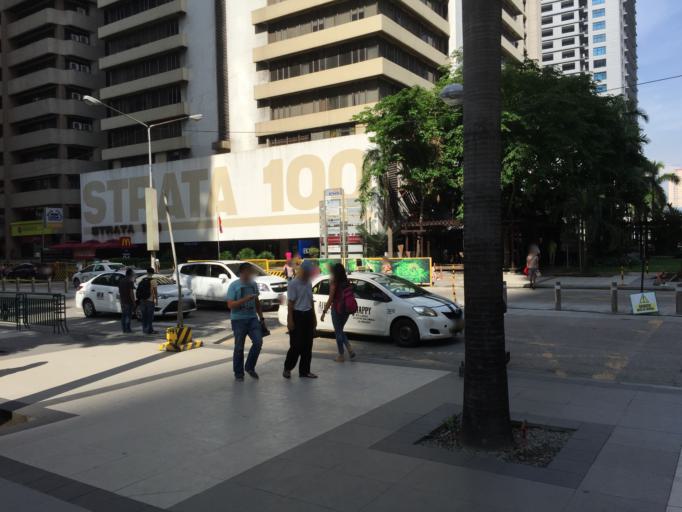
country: PH
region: Metro Manila
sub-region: Pasig
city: Pasig City
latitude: 14.5867
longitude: 121.0615
